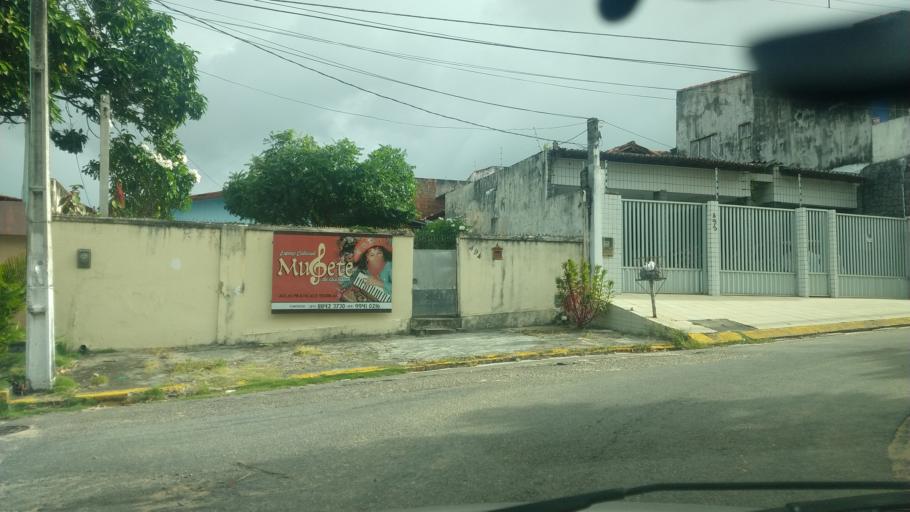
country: BR
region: Rio Grande do Norte
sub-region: Natal
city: Natal
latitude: -5.8278
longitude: -35.2076
